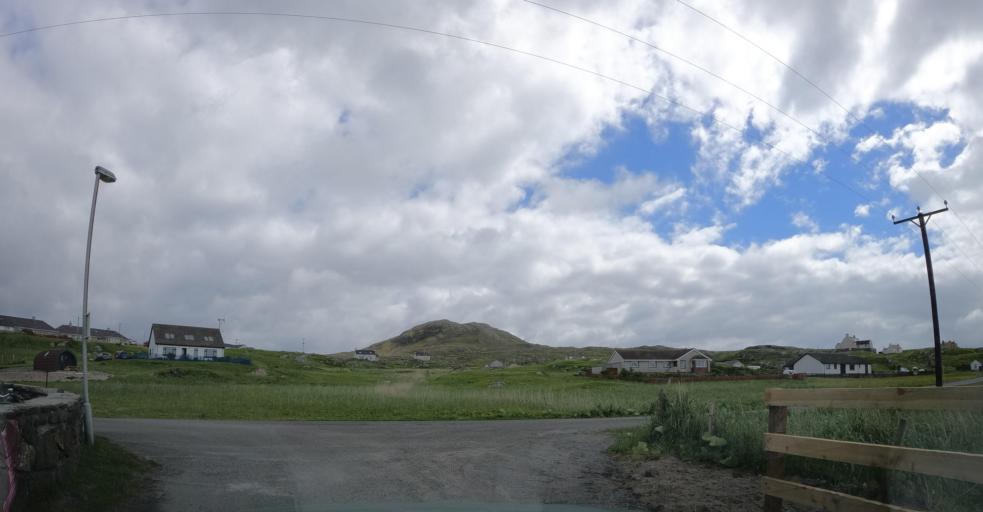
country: GB
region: Scotland
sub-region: Eilean Siar
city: Isle of South Uist
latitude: 57.0842
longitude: -7.3090
